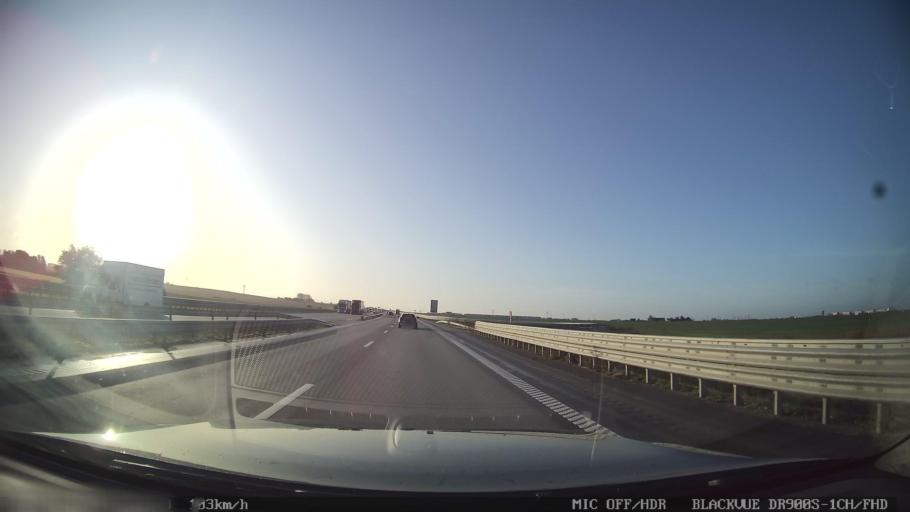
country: SE
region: Skane
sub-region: Landskrona
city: Landskrona
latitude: 55.8945
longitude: 12.8695
